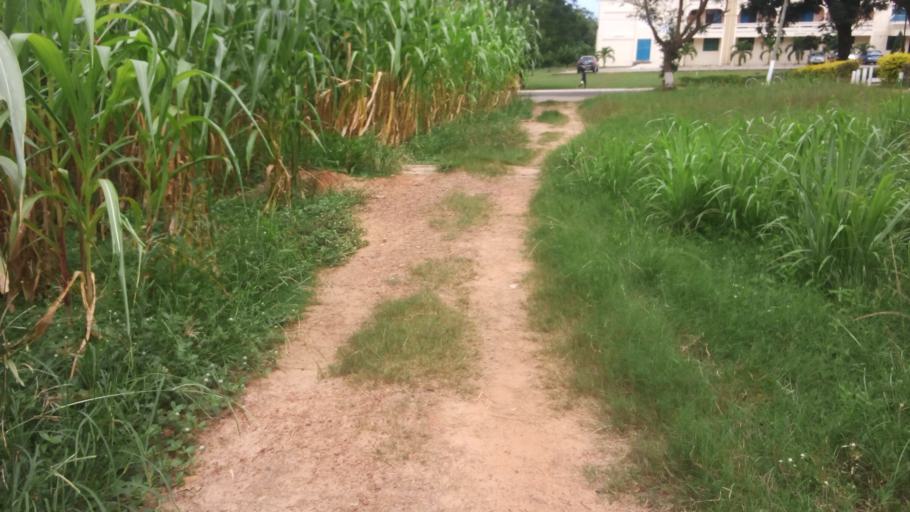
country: GH
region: Central
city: Cape Coast
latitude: 5.1185
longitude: -1.2889
